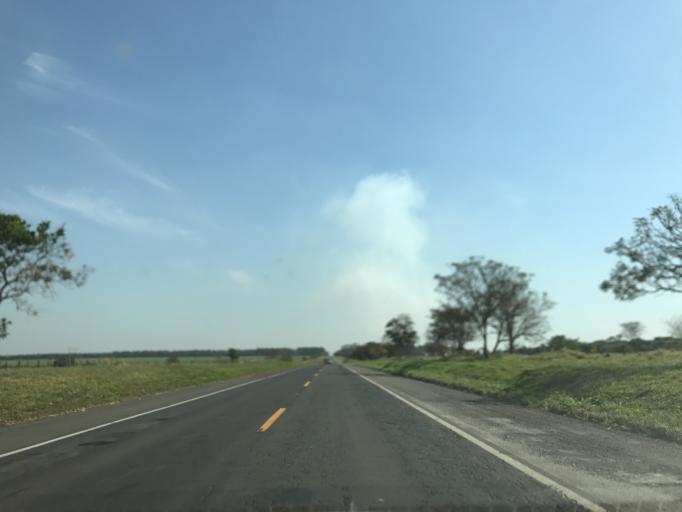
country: BR
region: Sao Paulo
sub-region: Penapolis
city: Penapolis
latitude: -21.3658
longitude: -50.0736
